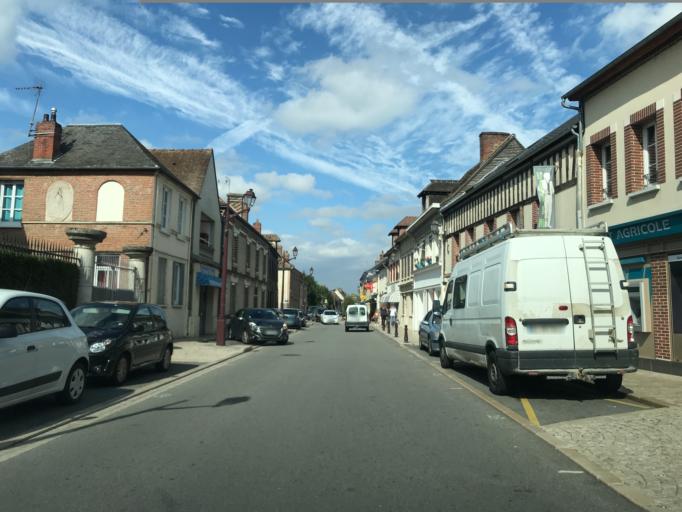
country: FR
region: Haute-Normandie
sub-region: Departement de l'Eure
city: Le Vaudreuil
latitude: 49.2569
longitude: 1.2093
